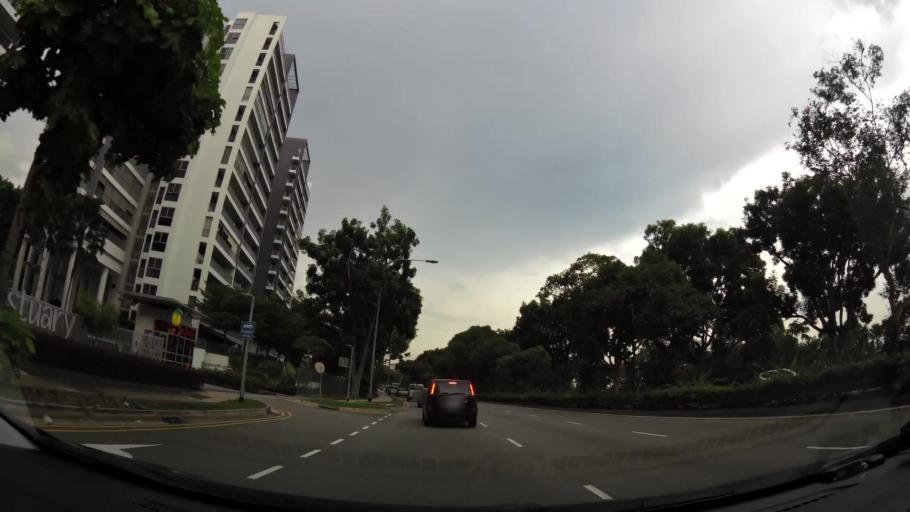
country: MY
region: Johor
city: Kampung Pasir Gudang Baru
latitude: 1.4104
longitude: 103.8320
